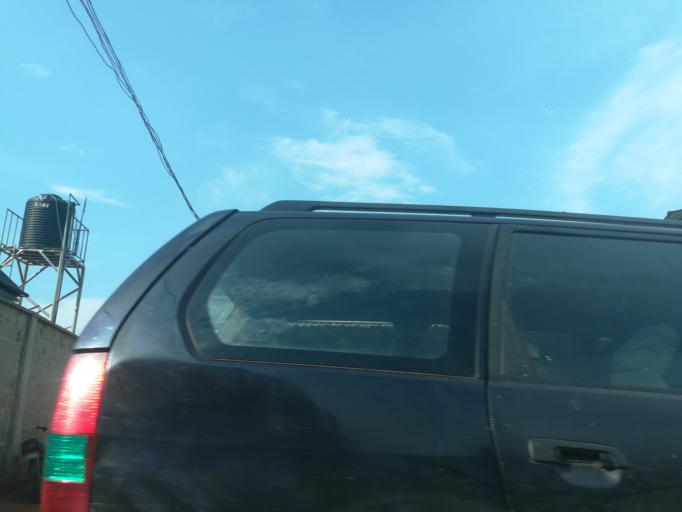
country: NG
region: Lagos
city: Ikorodu
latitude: 6.6222
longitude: 3.5019
